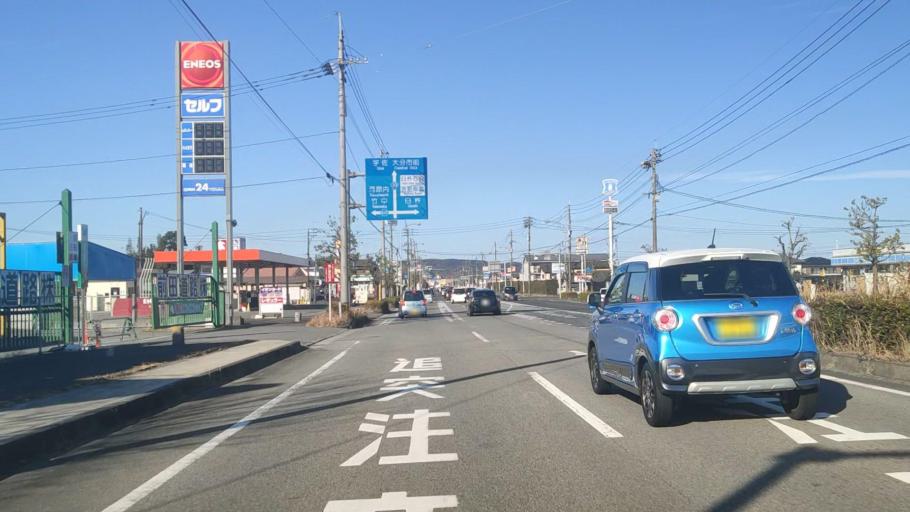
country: JP
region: Oita
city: Oita
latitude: 33.1414
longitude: 131.6580
